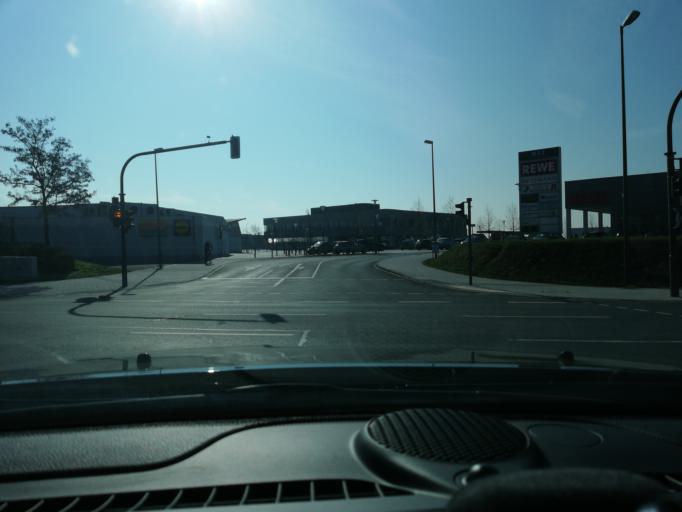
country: DE
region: Bavaria
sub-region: Regierungsbezirk Mittelfranken
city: Hessdorf
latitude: 49.5953
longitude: 10.9487
